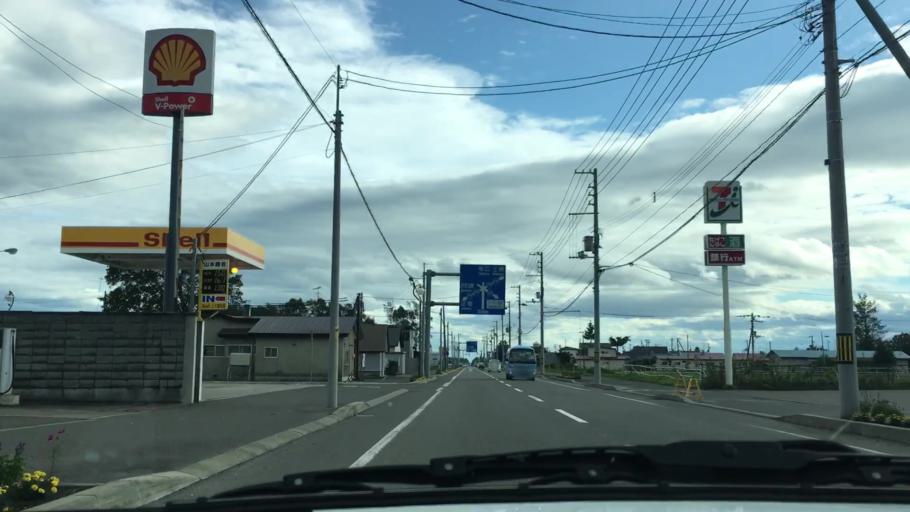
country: JP
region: Hokkaido
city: Otofuke
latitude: 43.2285
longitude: 143.2941
